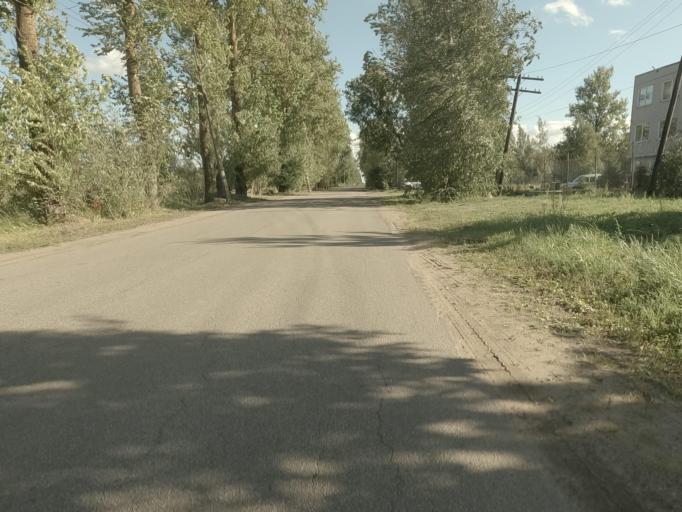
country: RU
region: Leningrad
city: Imeni Morozova
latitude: 59.9692
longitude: 31.0279
